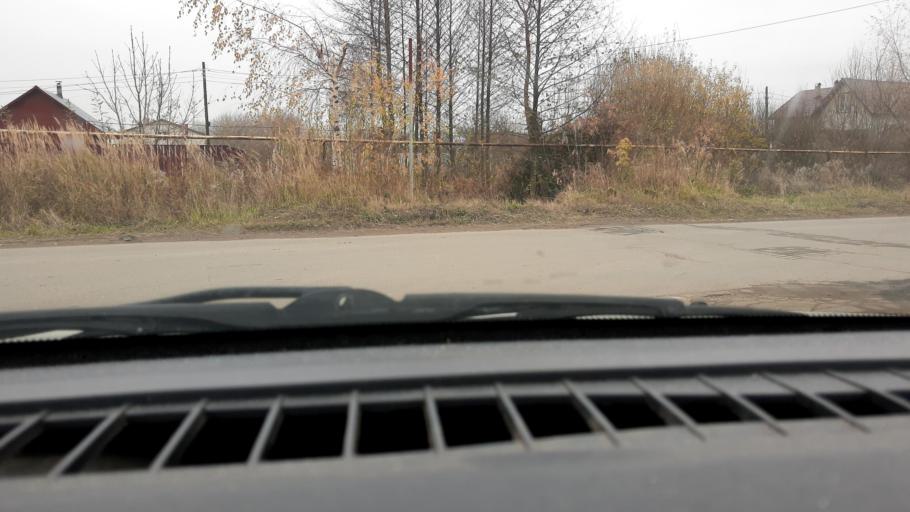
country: RU
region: Nizjnij Novgorod
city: Afonino
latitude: 56.2069
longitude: 44.0977
